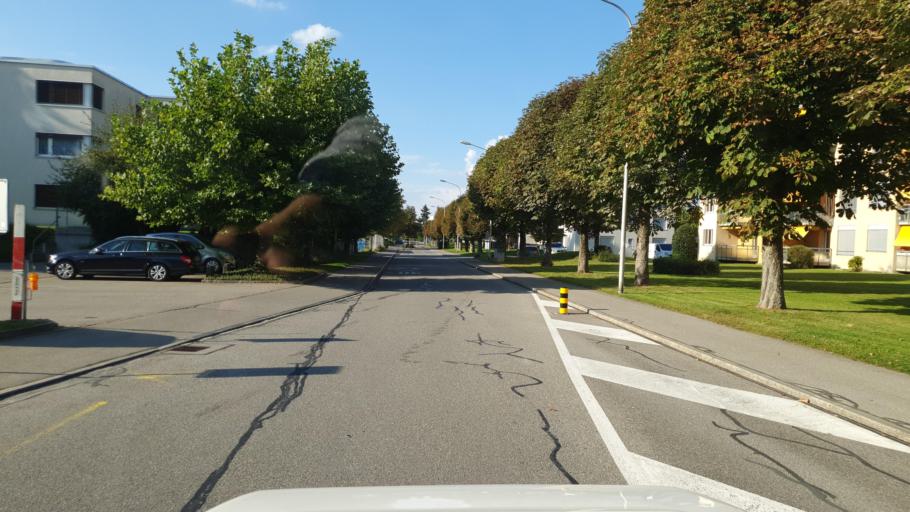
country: CH
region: Aargau
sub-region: Bezirk Muri
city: Muri
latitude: 47.2726
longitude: 8.3459
